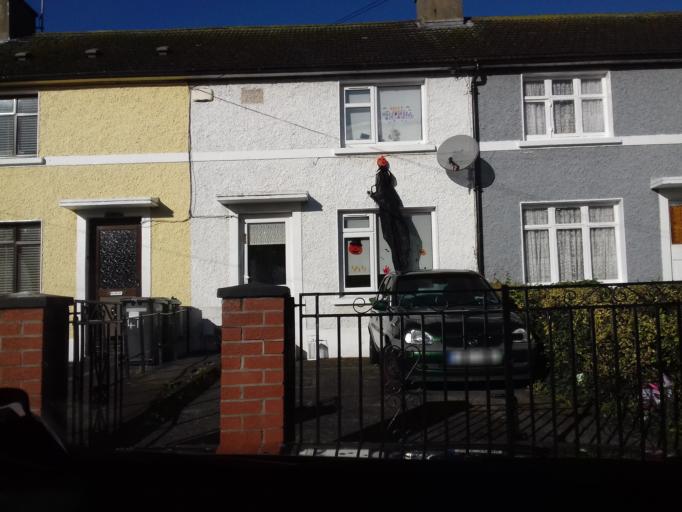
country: IE
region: Leinster
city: Cabra
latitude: 53.3698
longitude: -6.2968
